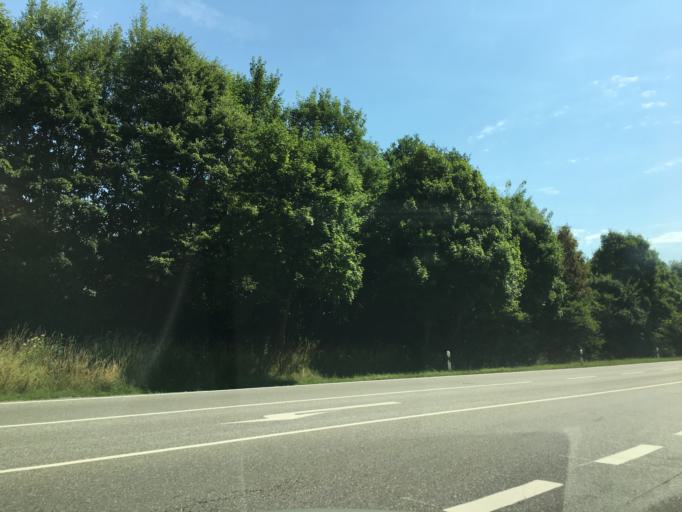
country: DE
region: Bavaria
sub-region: Upper Bavaria
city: Wasserburg am Inn
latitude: 48.0633
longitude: 12.2010
